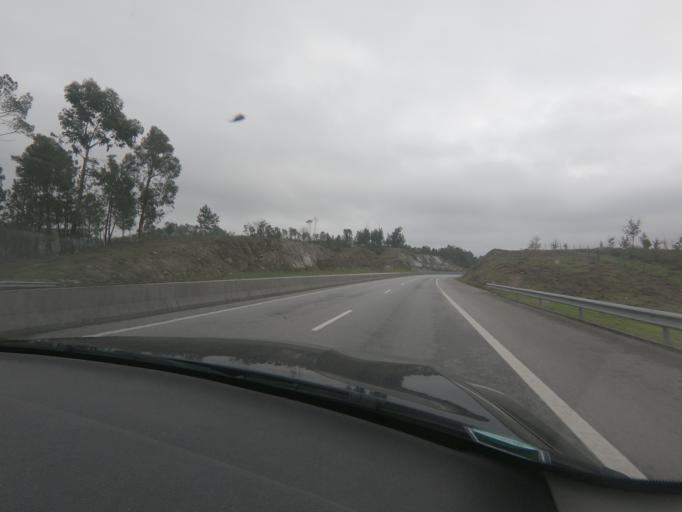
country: PT
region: Viseu
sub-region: Viseu
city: Viseu
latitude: 40.6403
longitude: -7.9598
